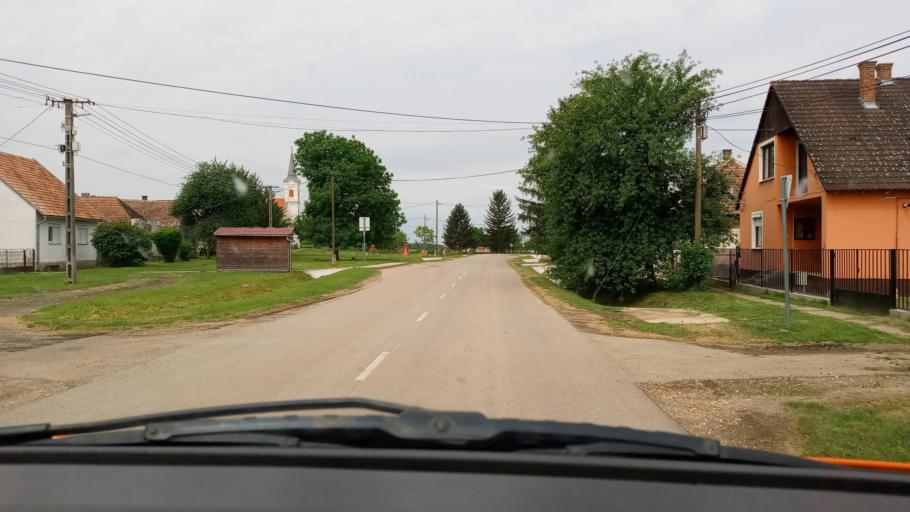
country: HU
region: Baranya
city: Vajszlo
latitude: 45.9082
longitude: 18.0327
